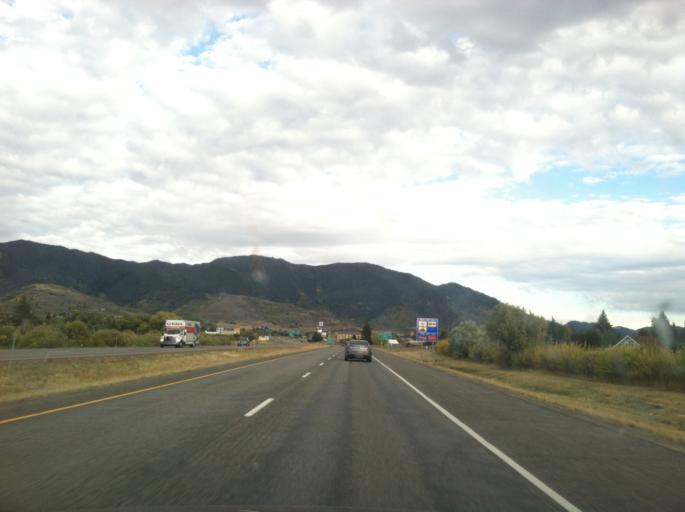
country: US
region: Montana
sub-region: Silver Bow County
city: Butte
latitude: 45.9879
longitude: -112.5201
